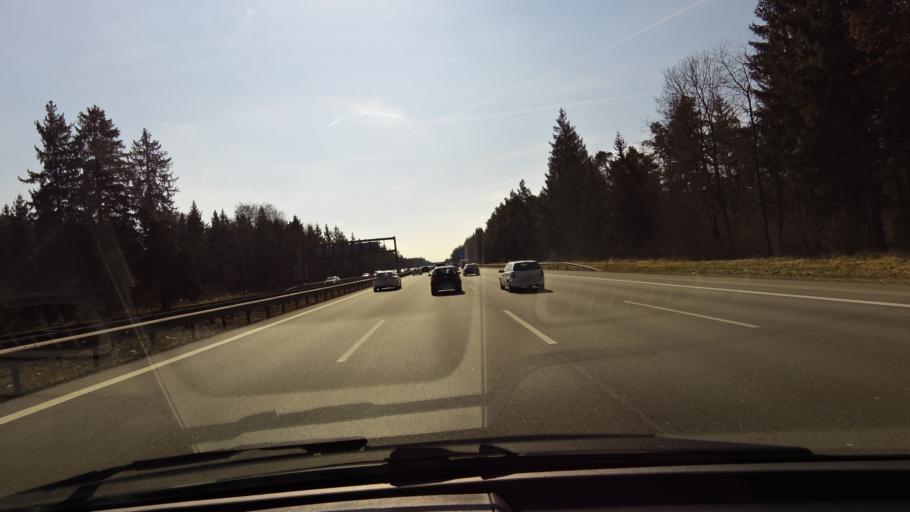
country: DE
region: Bavaria
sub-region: Upper Bavaria
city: Brunnthal
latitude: 47.9844
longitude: 11.6826
